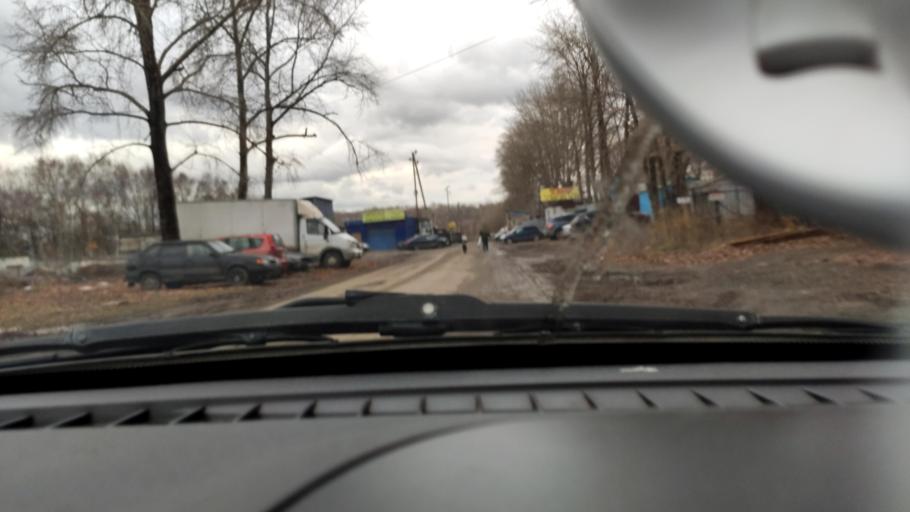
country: RU
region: Perm
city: Perm
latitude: 57.9655
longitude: 56.2030
